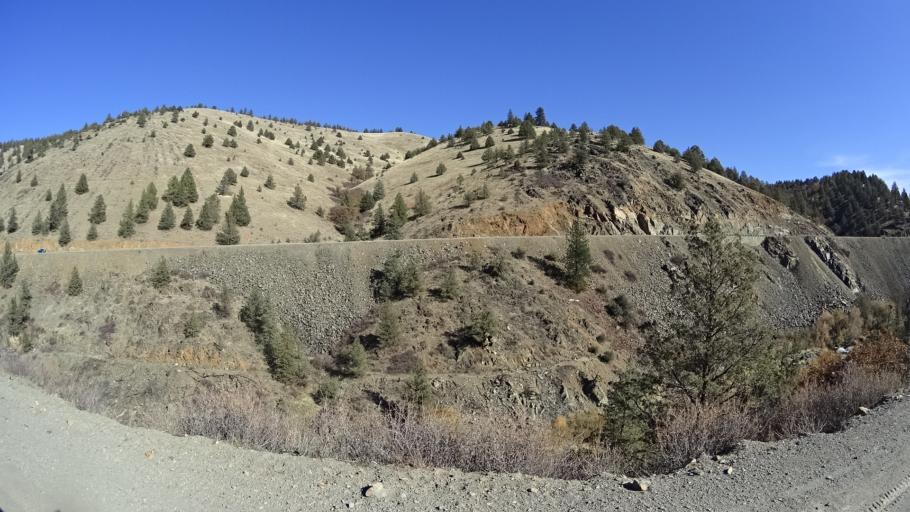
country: US
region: California
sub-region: Siskiyou County
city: Yreka
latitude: 41.7877
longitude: -122.6040
